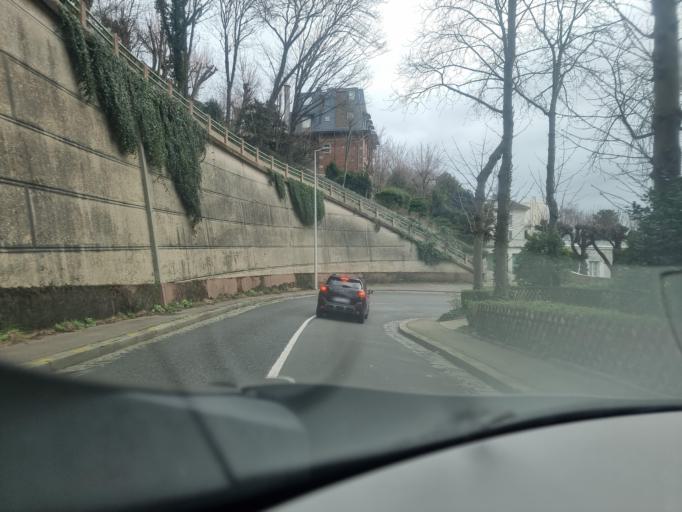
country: FR
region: Haute-Normandie
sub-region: Departement de la Seine-Maritime
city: Le Havre
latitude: 49.4991
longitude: 0.1013
